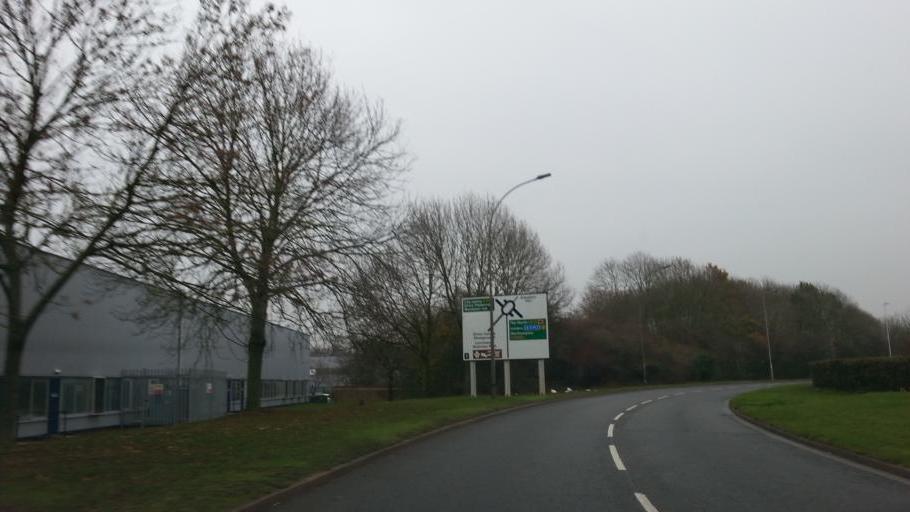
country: GB
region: England
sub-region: Cambridgeshire
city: Yaxley
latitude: 52.5379
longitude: -0.3058
